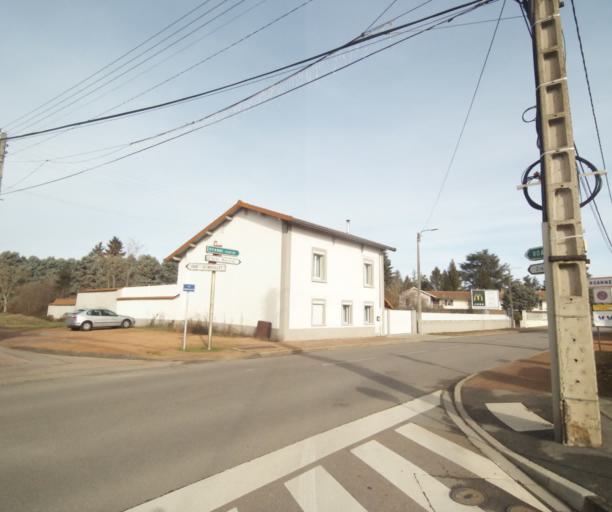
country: FR
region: Rhone-Alpes
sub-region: Departement de la Loire
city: Roanne
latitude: 46.0214
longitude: 4.0503
